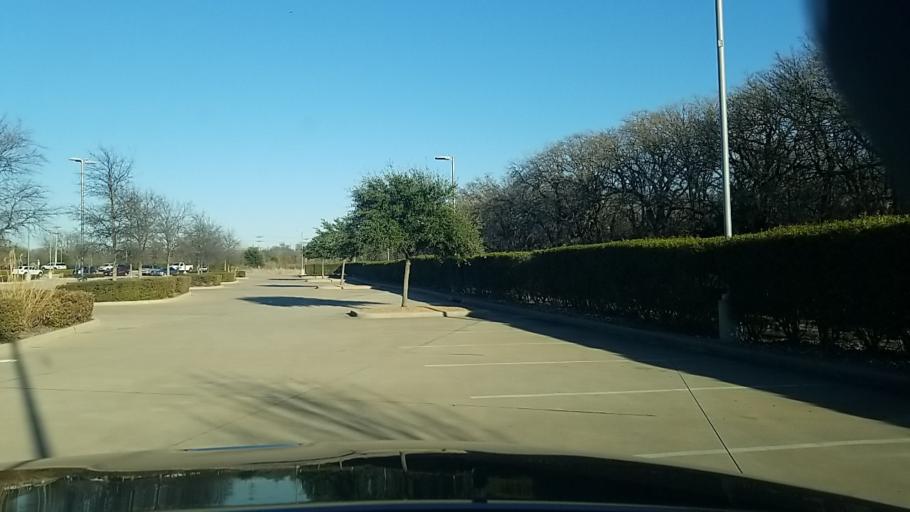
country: US
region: Texas
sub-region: Denton County
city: Corinth
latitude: 33.1814
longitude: -97.0913
